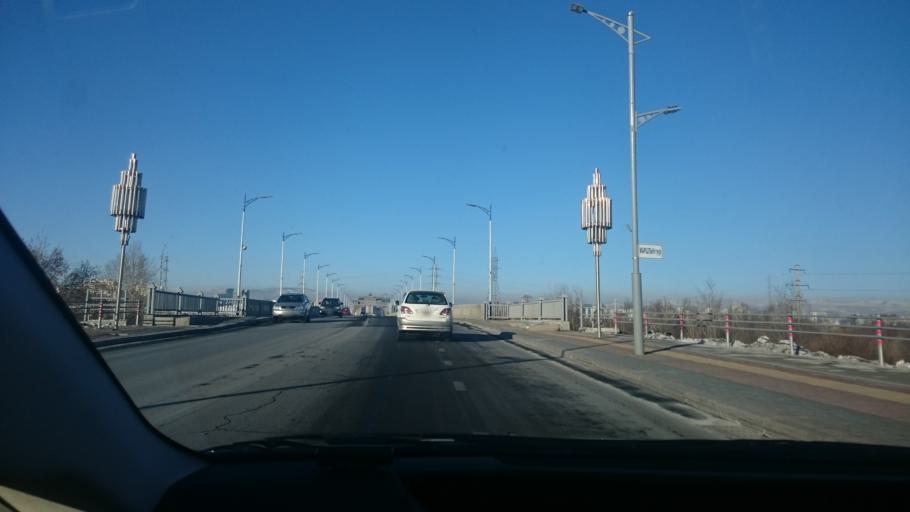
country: MN
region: Ulaanbaatar
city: Ulaanbaatar
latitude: 47.8857
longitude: 106.9400
